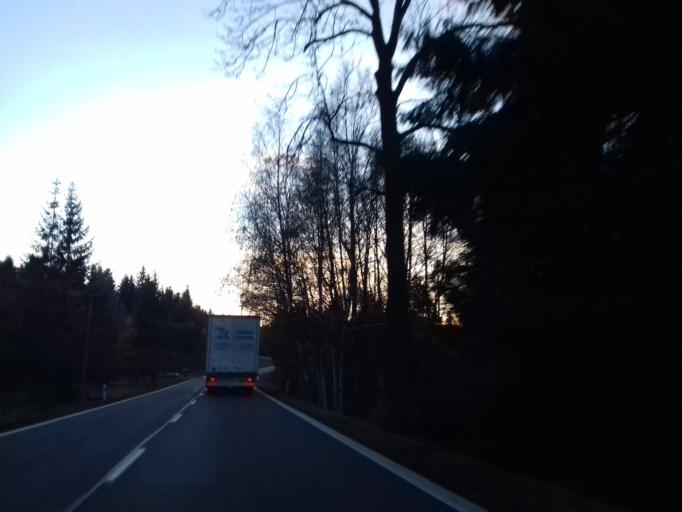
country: CZ
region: Vysocina
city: Krizova
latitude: 49.6887
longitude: 15.7919
